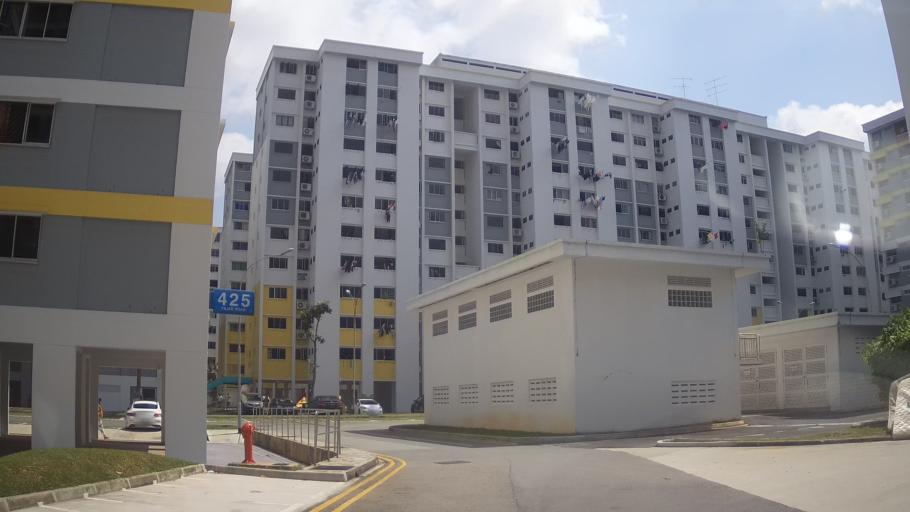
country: MY
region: Johor
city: Johor Bahru
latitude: 1.3855
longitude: 103.7695
